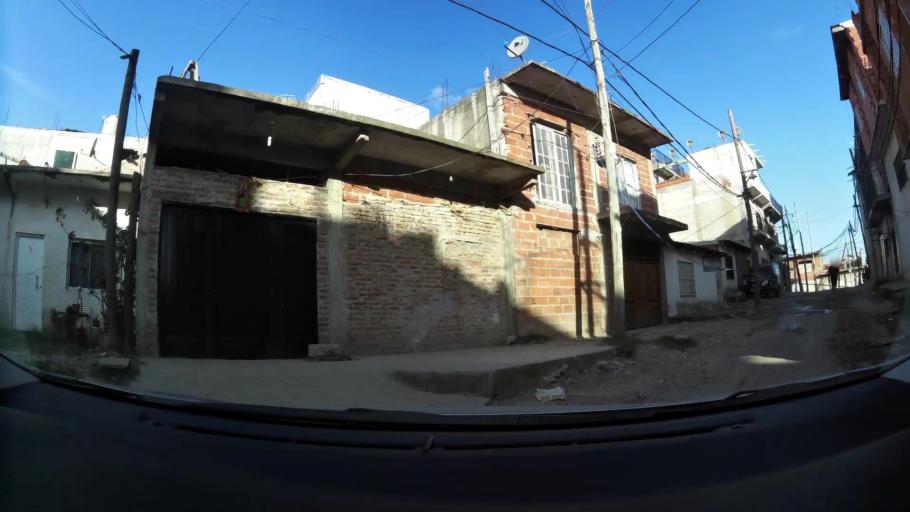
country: AR
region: Buenos Aires F.D.
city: Villa Lugano
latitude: -34.7076
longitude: -58.4828
